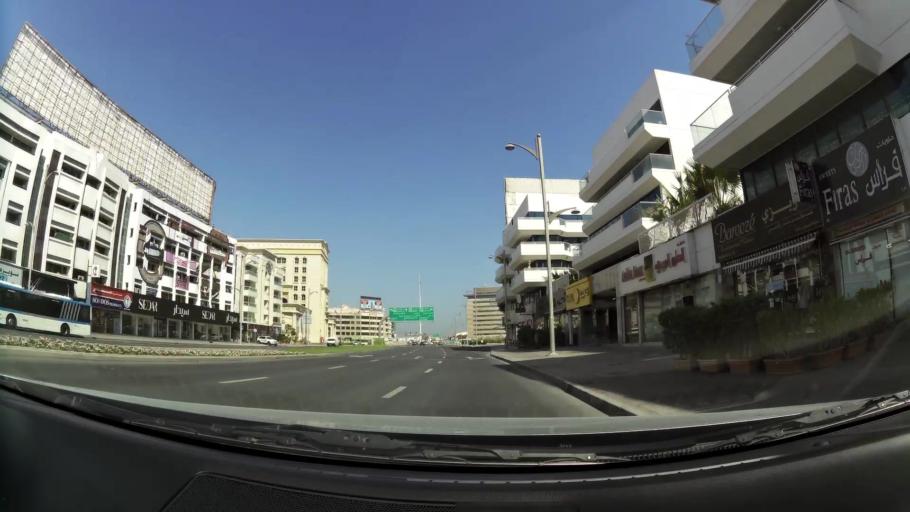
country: AE
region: Ash Shariqah
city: Sharjah
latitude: 25.2378
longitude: 55.2749
